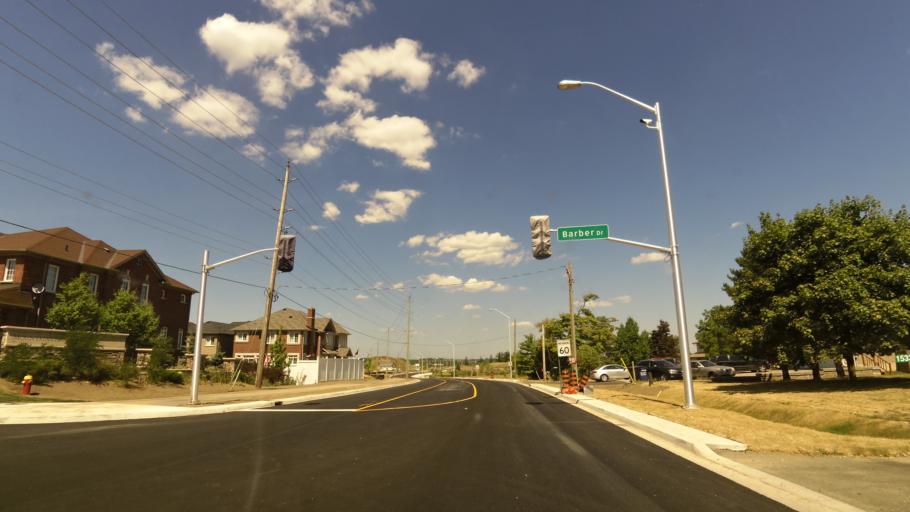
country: CA
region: Ontario
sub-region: Halton
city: Milton
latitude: 43.6310
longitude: -79.8696
